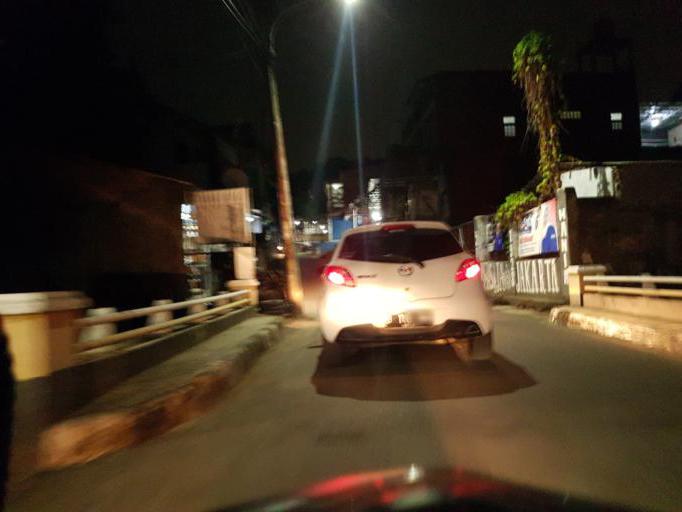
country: ID
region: West Java
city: Cileungsir
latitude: -6.3154
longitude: 106.9148
